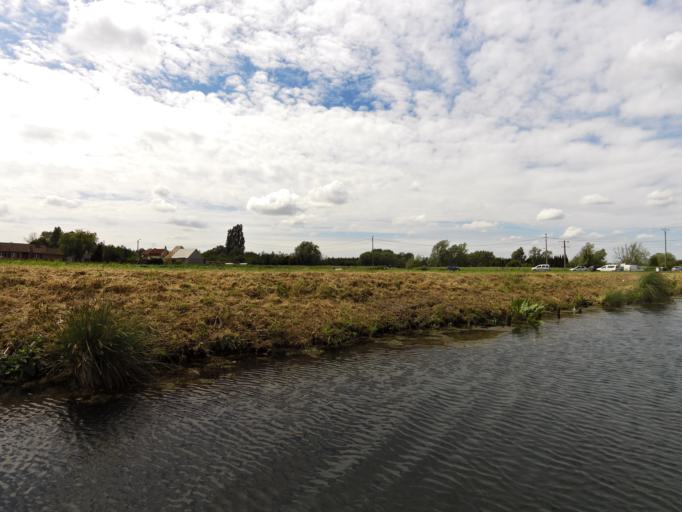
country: FR
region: Nord-Pas-de-Calais
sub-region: Departement du Pas-de-Calais
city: Saint-Martin-au-Laert
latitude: 50.7607
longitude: 2.2448
